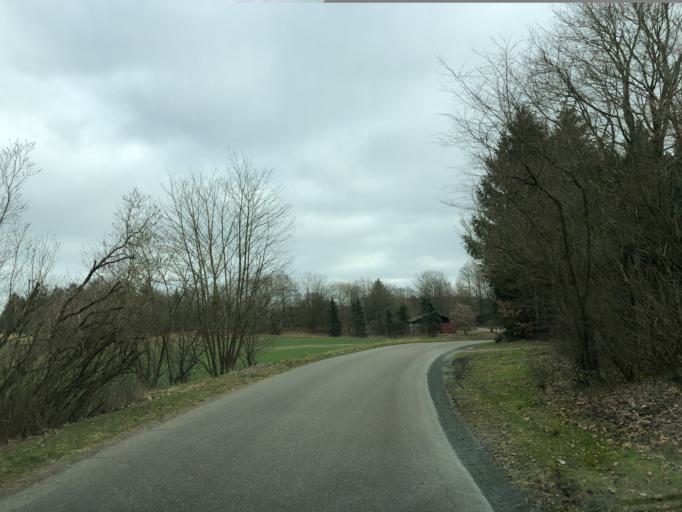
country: DK
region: South Denmark
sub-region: Billund Kommune
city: Billund
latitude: 55.7830
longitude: 9.1670
